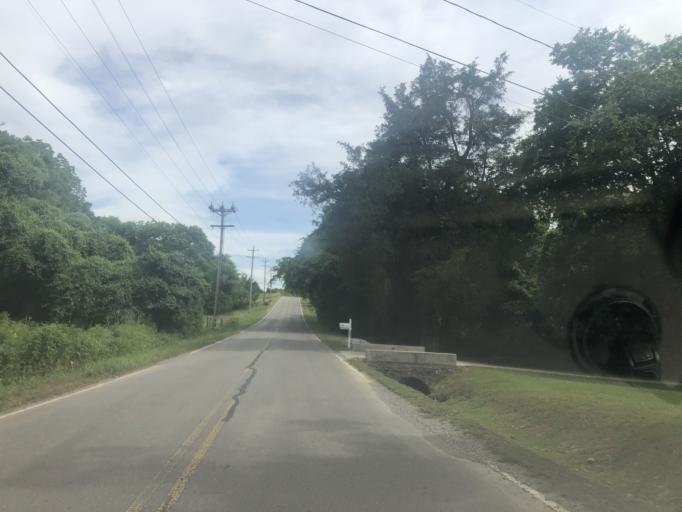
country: US
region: Tennessee
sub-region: Davidson County
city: Lakewood
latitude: 36.2173
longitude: -86.6670
